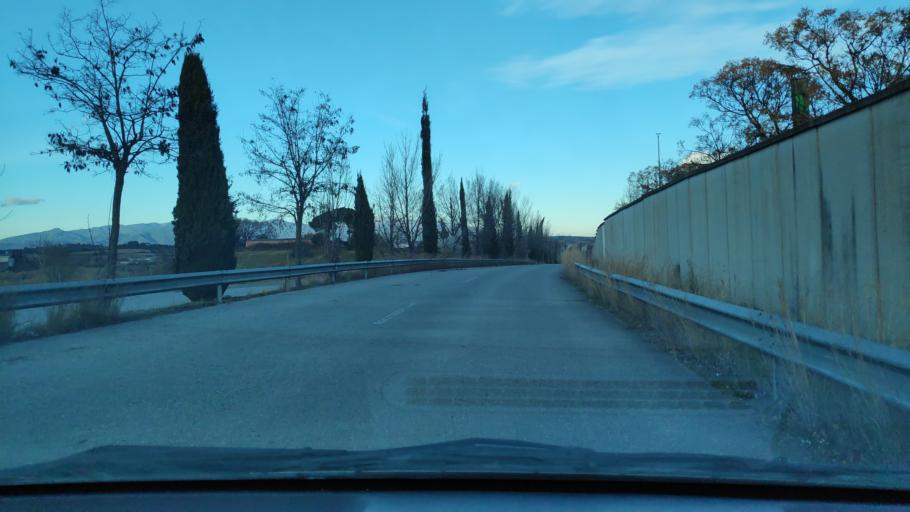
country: ES
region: Catalonia
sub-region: Provincia de Barcelona
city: Llica de Vall
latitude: 41.5743
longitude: 2.2584
